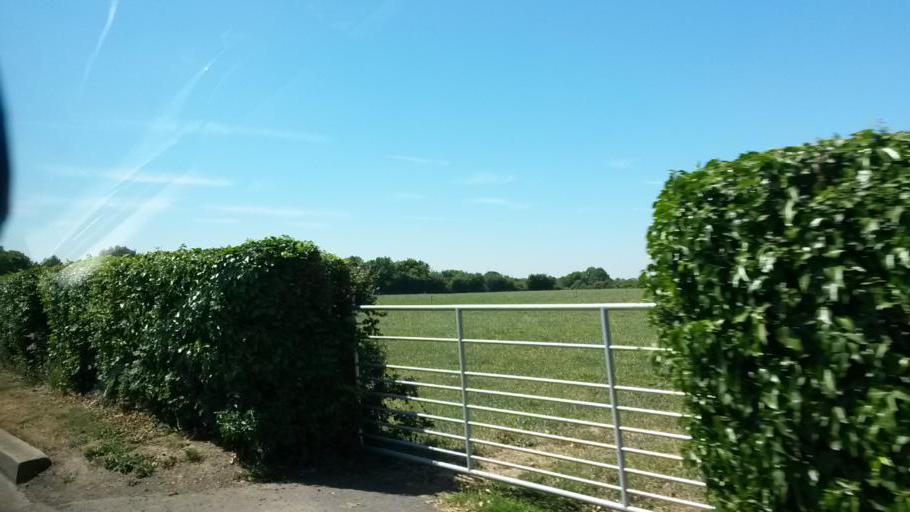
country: IE
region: Leinster
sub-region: Fingal County
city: Swords
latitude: 53.5141
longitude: -6.2674
